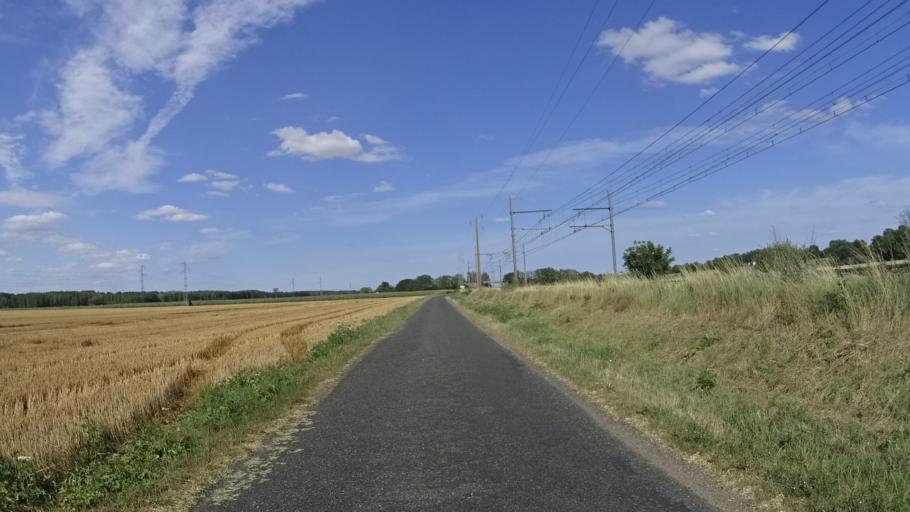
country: FR
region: Centre
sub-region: Departement d'Indre-et-Loire
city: Cangey
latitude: 47.4657
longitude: 1.0868
